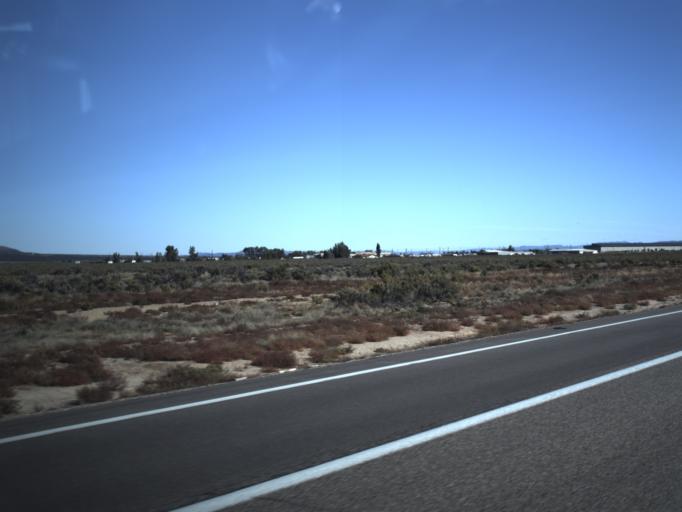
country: US
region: Utah
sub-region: Iron County
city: Cedar City
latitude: 37.6786
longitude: -113.1751
